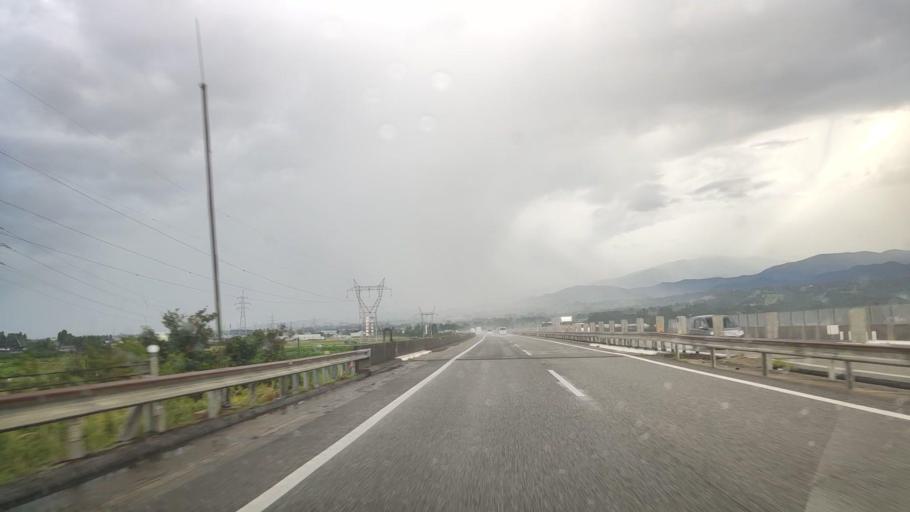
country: JP
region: Toyama
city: Kamiichi
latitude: 36.7243
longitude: 137.3609
